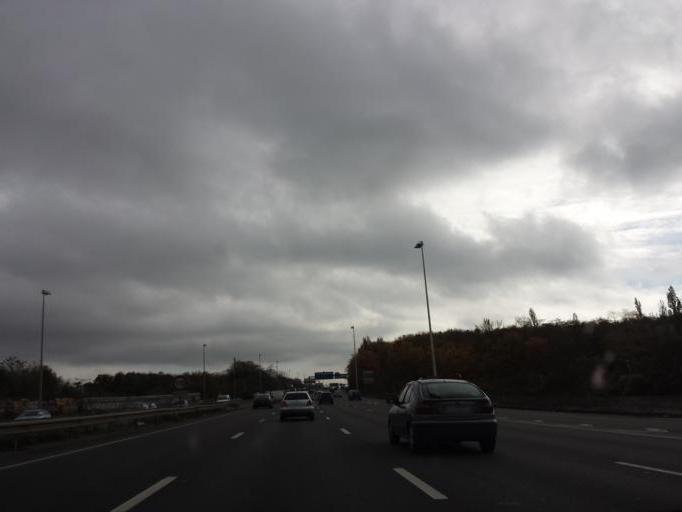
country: FR
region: Ile-de-France
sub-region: Departement du Val-d'Oise
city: Sannois
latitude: 48.9637
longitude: 2.2637
